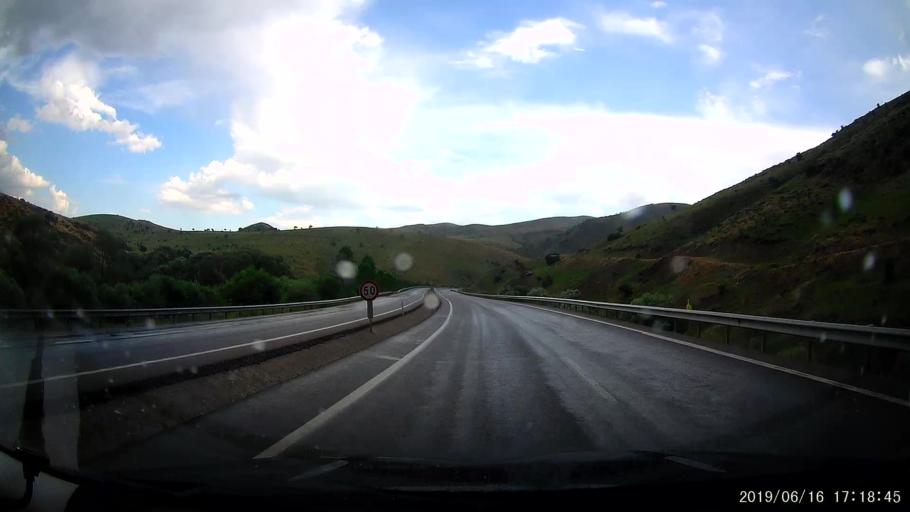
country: TR
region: Erzincan
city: Tercan
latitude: 39.8094
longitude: 40.5296
